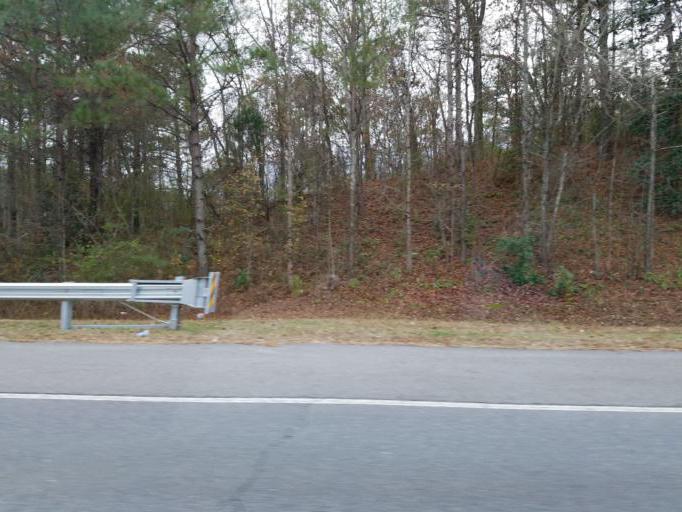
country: US
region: Georgia
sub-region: Cherokee County
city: Canton
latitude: 34.2208
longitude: -84.4959
